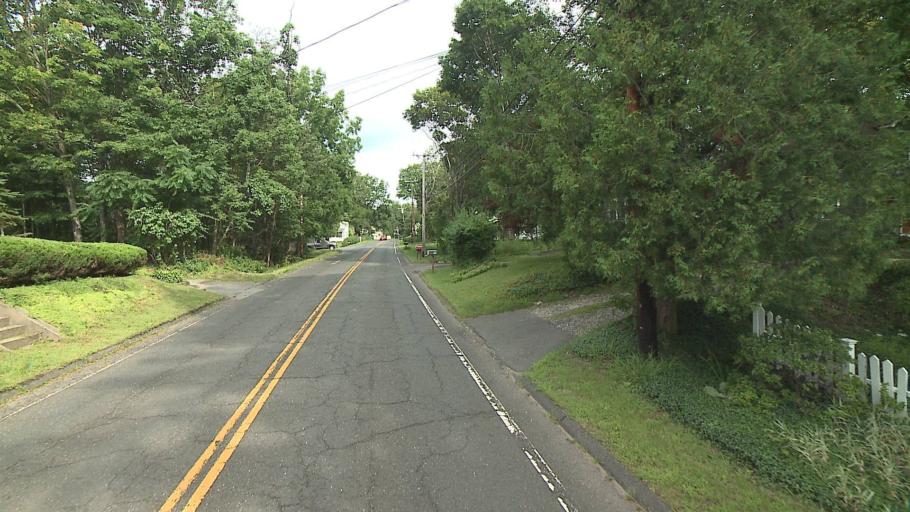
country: US
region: Connecticut
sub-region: Litchfield County
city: Woodbury
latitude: 41.5587
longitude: -73.2132
